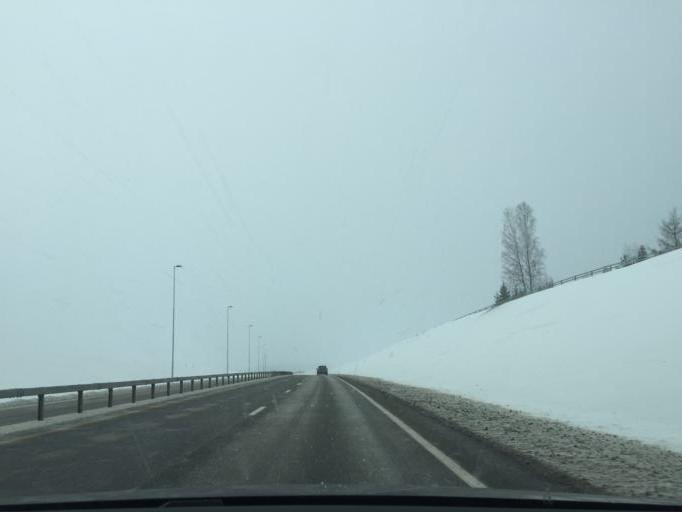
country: NO
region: Hedmark
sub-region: Sor-Odal
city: Skarnes
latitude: 60.2420
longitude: 11.7887
